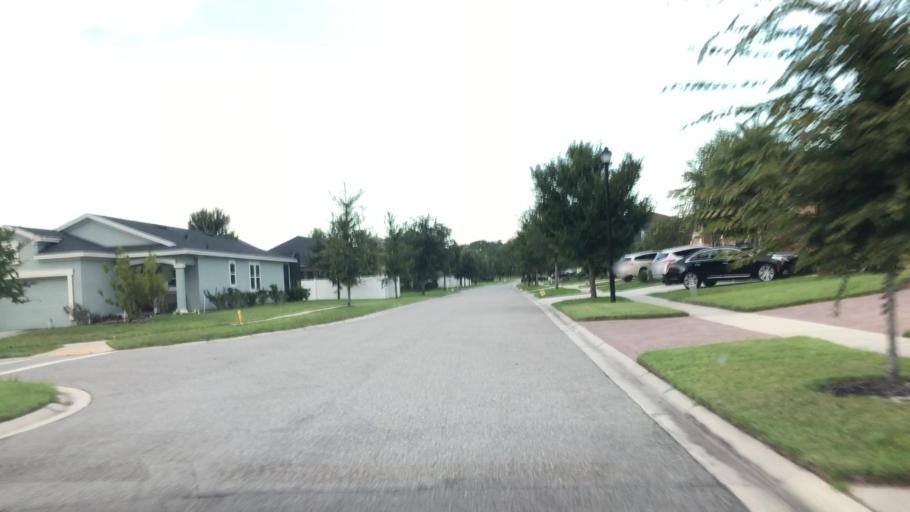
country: US
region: Florida
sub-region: Saint Johns County
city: Palm Valley
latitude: 30.0978
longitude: -81.4618
